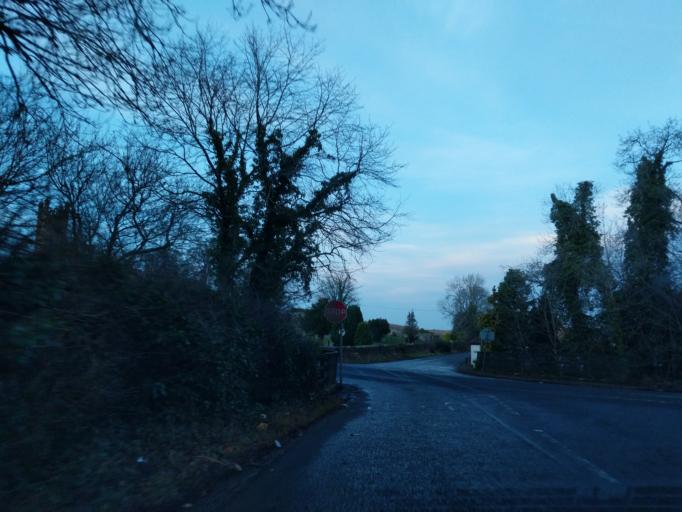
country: GB
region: Scotland
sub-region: Midlothian
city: Bonnyrigg
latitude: 55.8649
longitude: -3.0886
